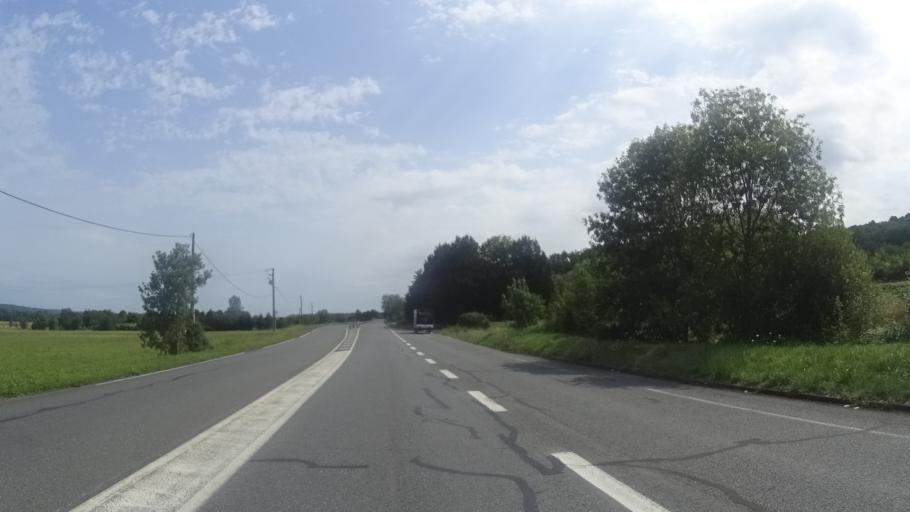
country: FR
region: Aquitaine
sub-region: Departement de la Dordogne
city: Sourzac
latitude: 45.0699
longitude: 0.4359
